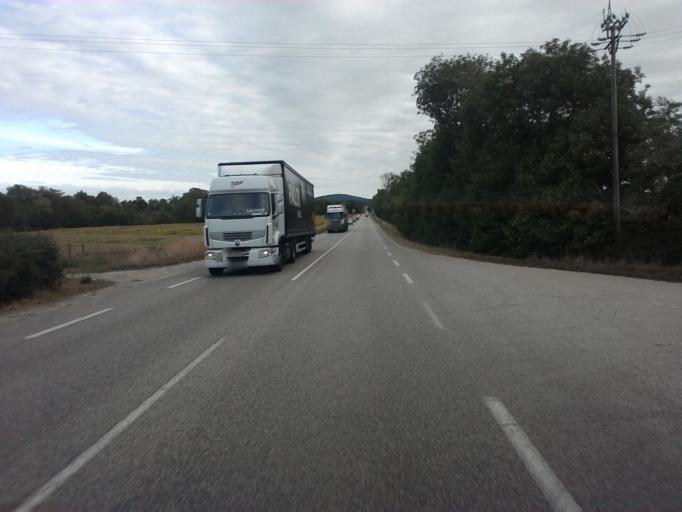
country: FR
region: Rhone-Alpes
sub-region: Departement de l'Ain
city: Ambronay
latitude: 46.0337
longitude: 5.3378
